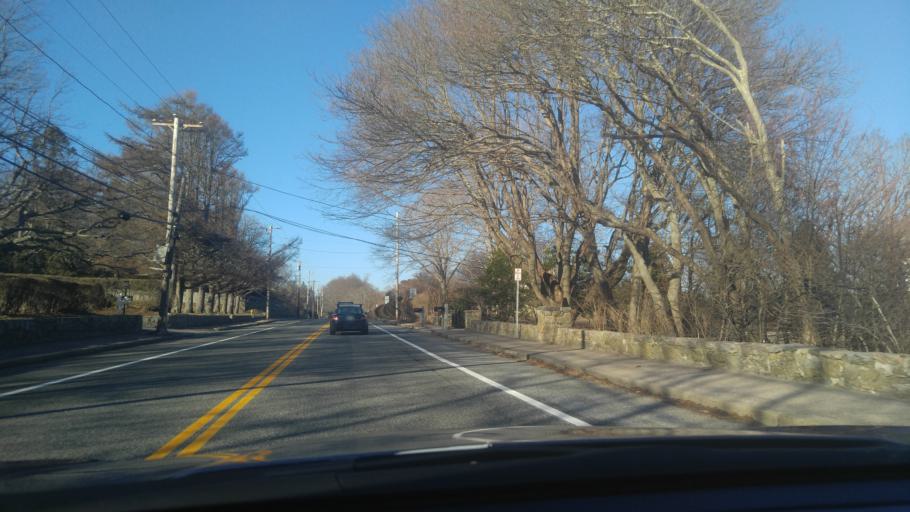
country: US
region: Rhode Island
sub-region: Washington County
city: Narragansett Pier
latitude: 41.4400
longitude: -71.4510
